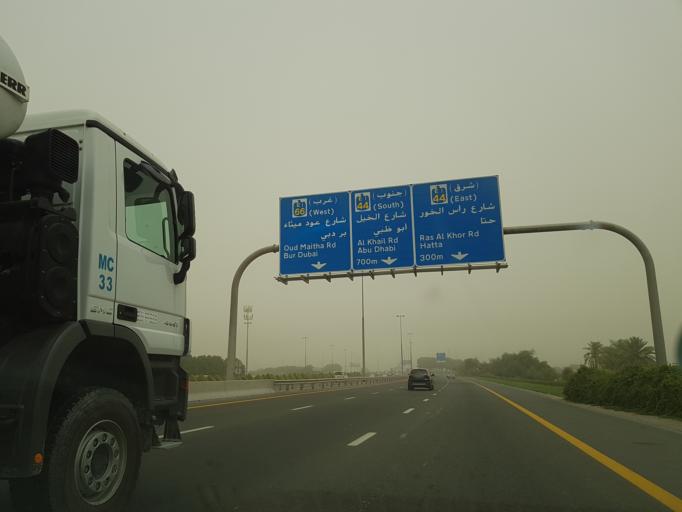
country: AE
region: Dubai
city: Dubai
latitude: 25.1766
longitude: 55.3196
